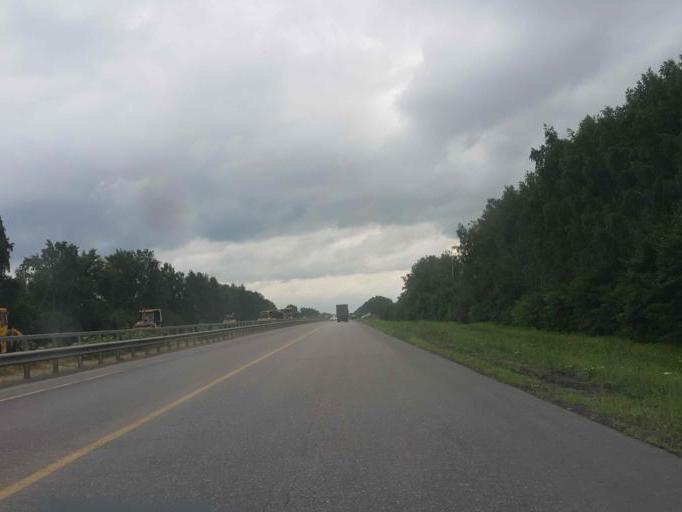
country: RU
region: Tambov
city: Selezni
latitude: 52.8061
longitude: 40.9681
